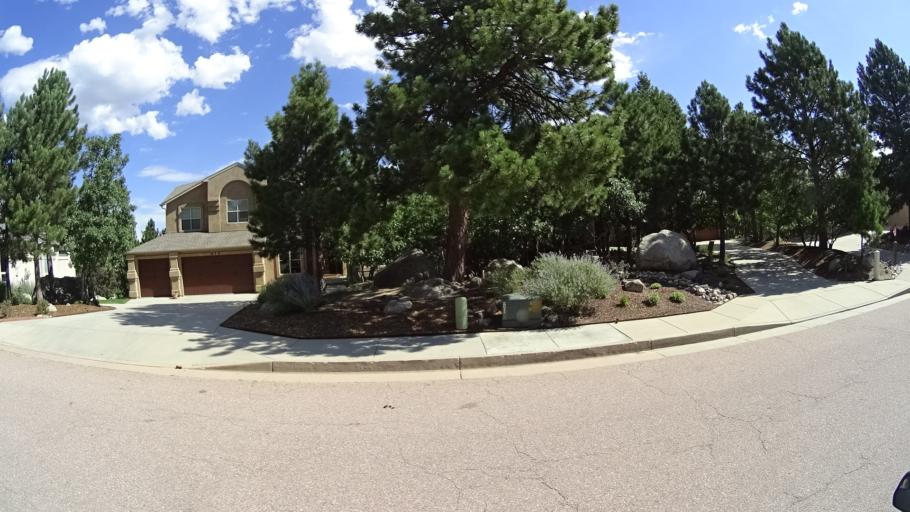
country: US
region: Colorado
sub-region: El Paso County
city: Fort Carson
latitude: 38.7434
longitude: -104.8345
